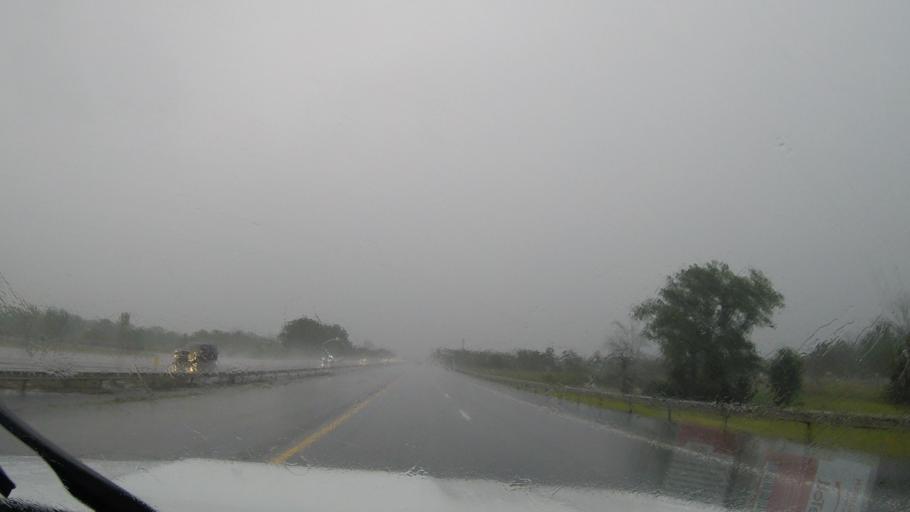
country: US
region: New York
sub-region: Ontario County
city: Phelps
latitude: 42.9549
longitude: -76.9838
